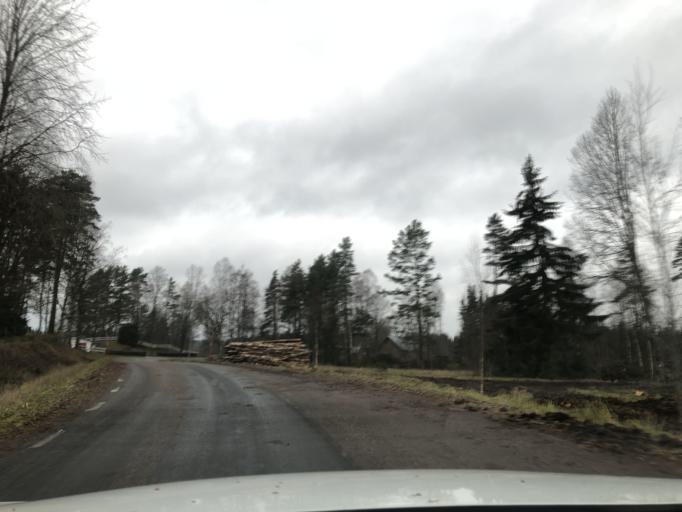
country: SE
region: Vaestra Goetaland
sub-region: Ulricehamns Kommun
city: Ulricehamn
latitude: 57.8663
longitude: 13.5512
